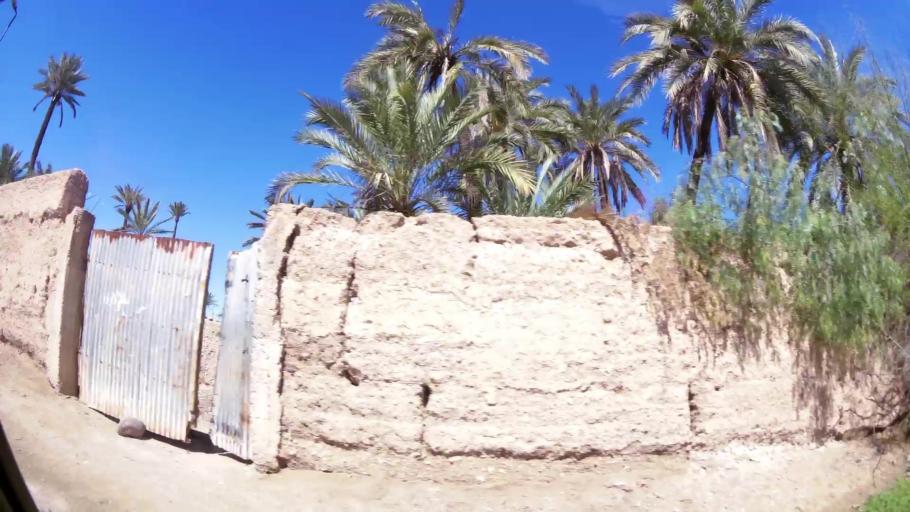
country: MA
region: Marrakech-Tensift-Al Haouz
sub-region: Marrakech
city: Marrakesh
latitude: 31.6758
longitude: -7.9738
